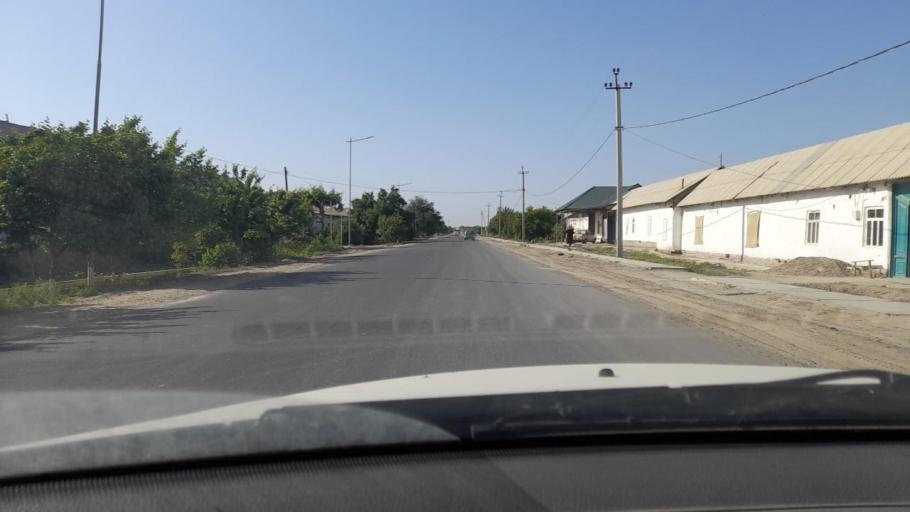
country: UZ
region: Bukhara
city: Romiton
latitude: 40.0744
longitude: 64.3263
